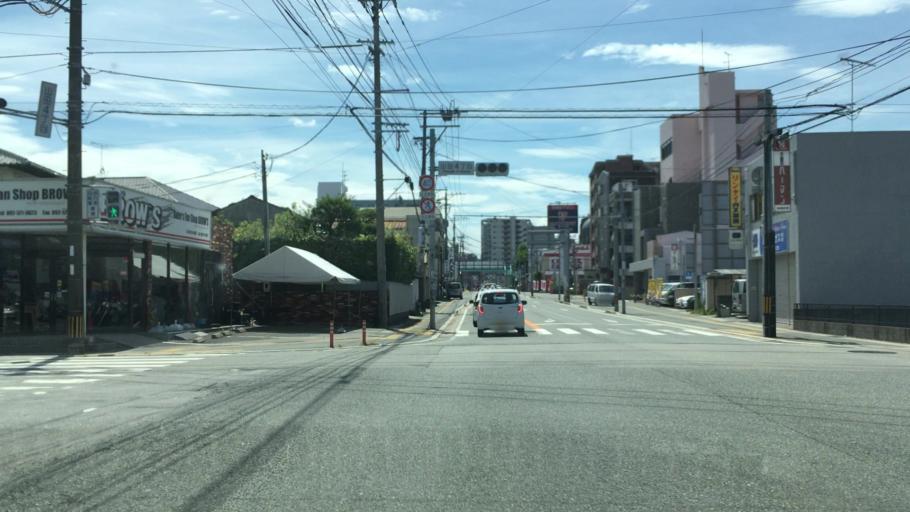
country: JP
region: Fukuoka
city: Onojo
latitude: 33.5441
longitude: 130.4714
